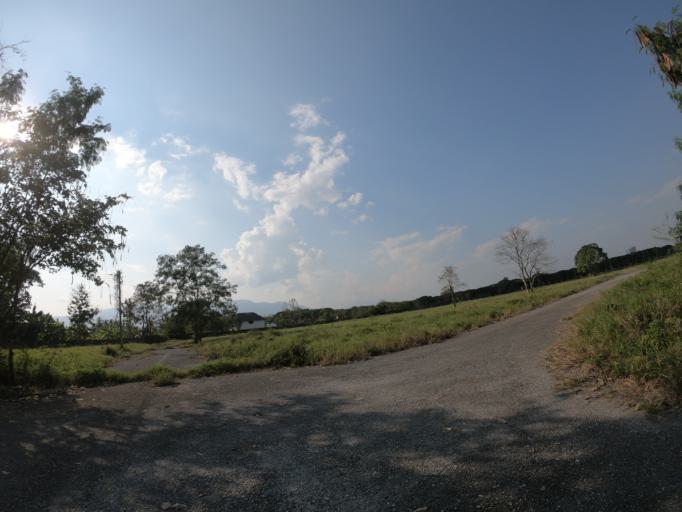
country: TH
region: Chiang Mai
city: Chiang Mai
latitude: 18.8328
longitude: 99.0007
